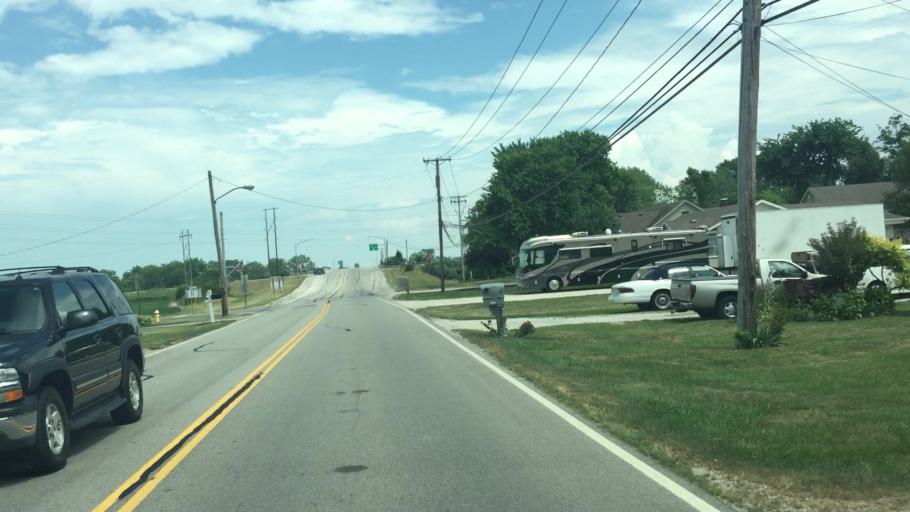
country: US
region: Ohio
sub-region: Wood County
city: Walbridge
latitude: 41.5879
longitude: -83.4818
